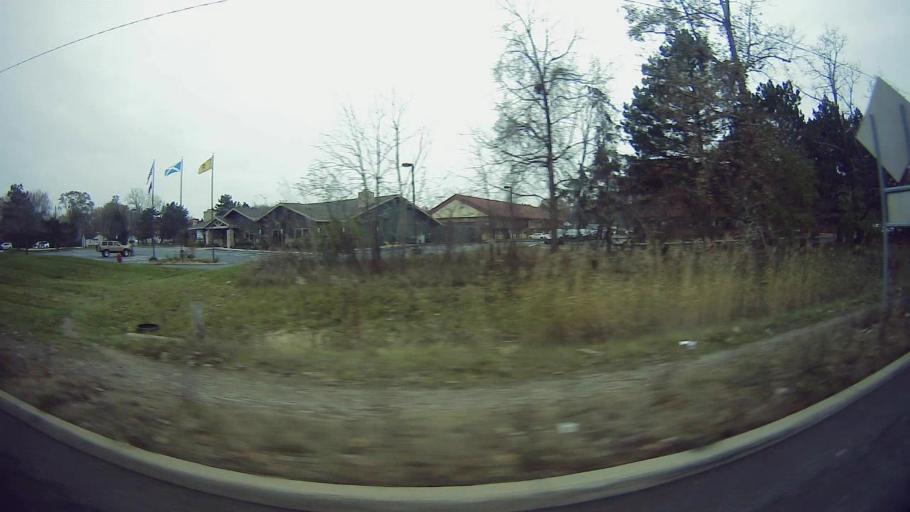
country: US
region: Michigan
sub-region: Oakland County
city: Clawson
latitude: 42.5564
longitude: -83.1285
